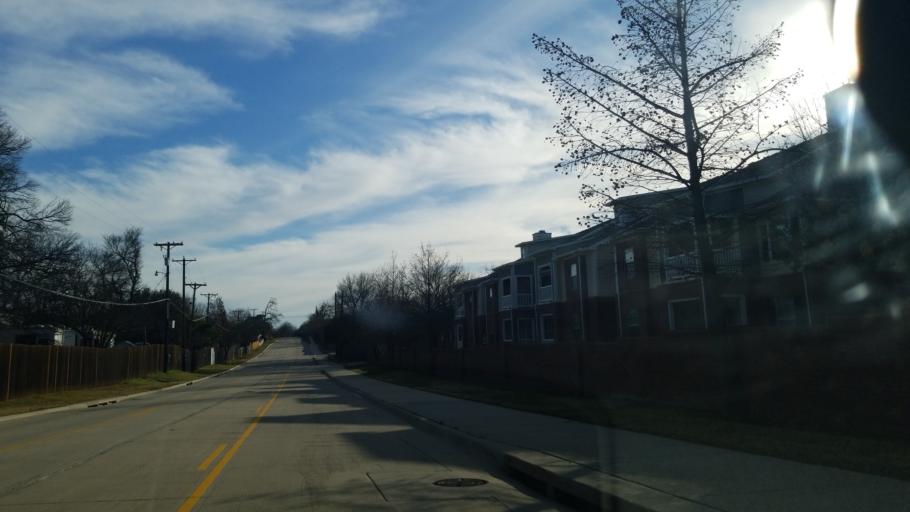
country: US
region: Texas
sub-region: Denton County
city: Corinth
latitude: 33.1406
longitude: -97.0559
